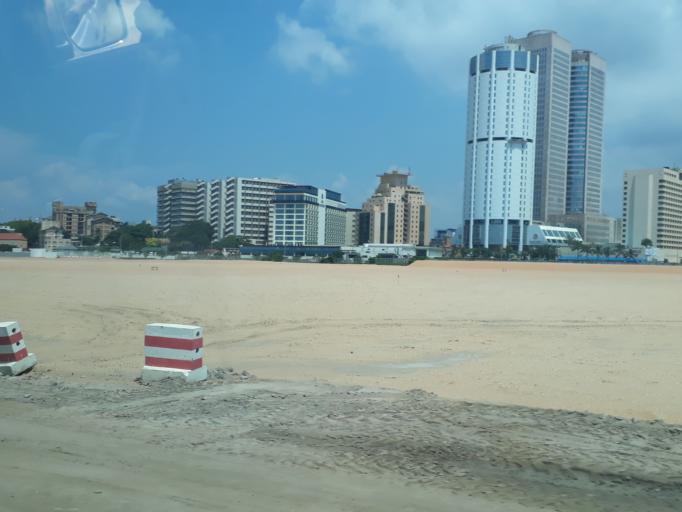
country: LK
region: Western
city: Colombo
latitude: 6.9304
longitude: 79.8394
